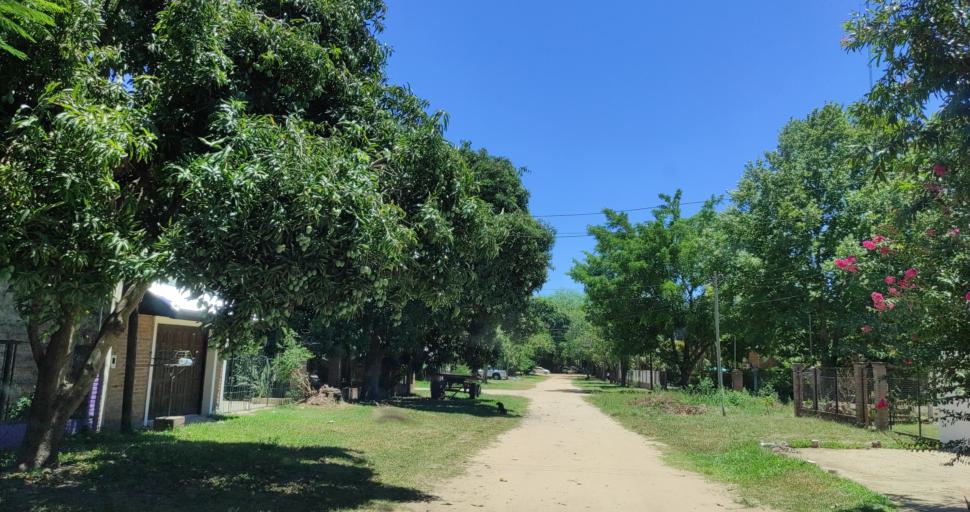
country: AR
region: Corrientes
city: Ituzaingo
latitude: -27.5902
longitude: -56.7009
